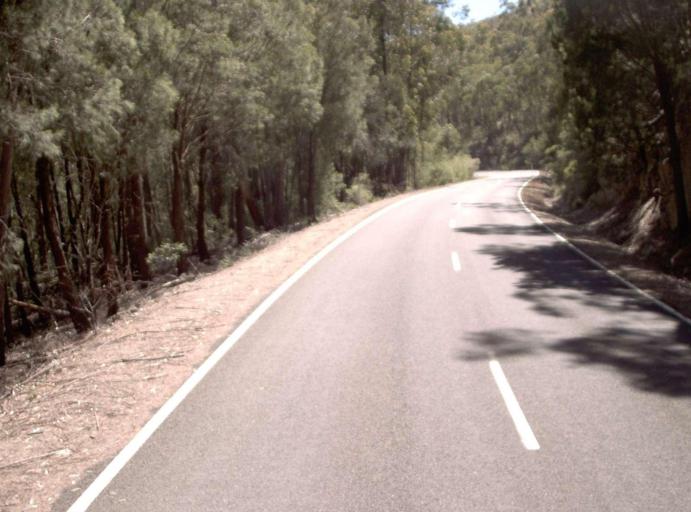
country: AU
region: Victoria
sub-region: East Gippsland
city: Lakes Entrance
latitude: -37.3745
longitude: 148.2179
